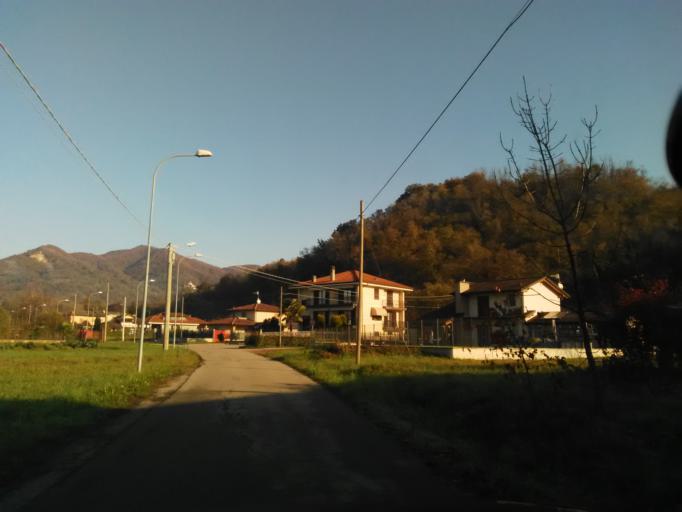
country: IT
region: Piedmont
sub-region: Provincia di Novara
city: Grignasco
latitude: 45.6750
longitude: 8.3523
